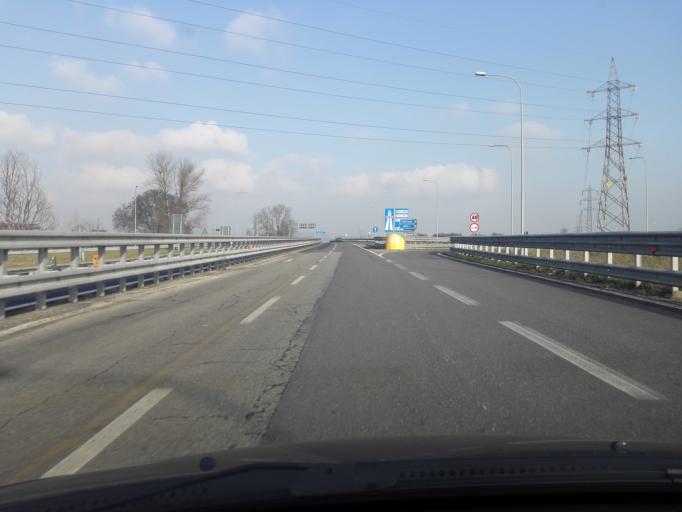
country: IT
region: Piedmont
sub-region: Provincia di Alessandria
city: Alessandria
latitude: 44.9050
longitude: 8.6394
